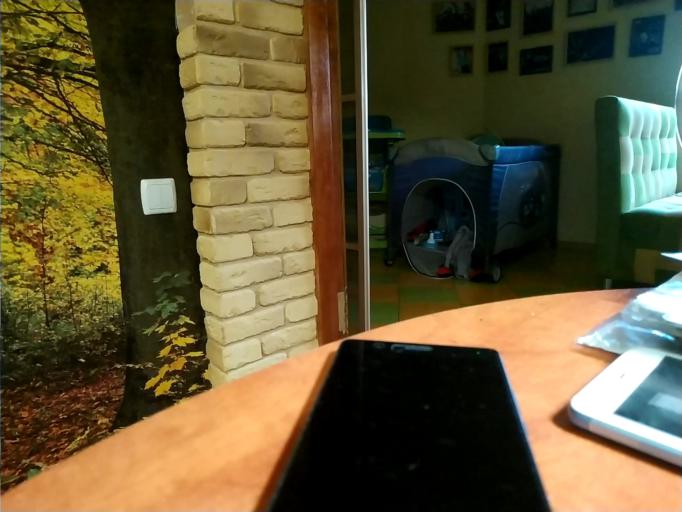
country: RU
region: Orjol
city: Znamenskoye
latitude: 53.5575
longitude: 35.4855
